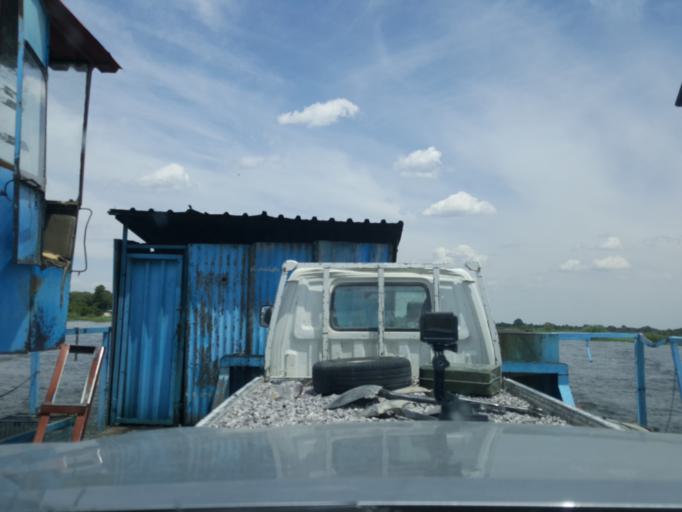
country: BW
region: North West
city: Shakawe
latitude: -18.2737
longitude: 21.7909
